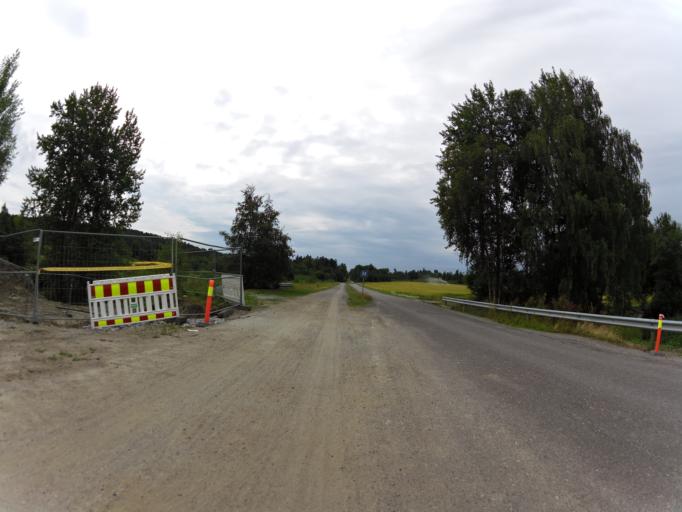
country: NO
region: Akershus
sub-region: As
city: As
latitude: 59.6761
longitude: 10.7454
